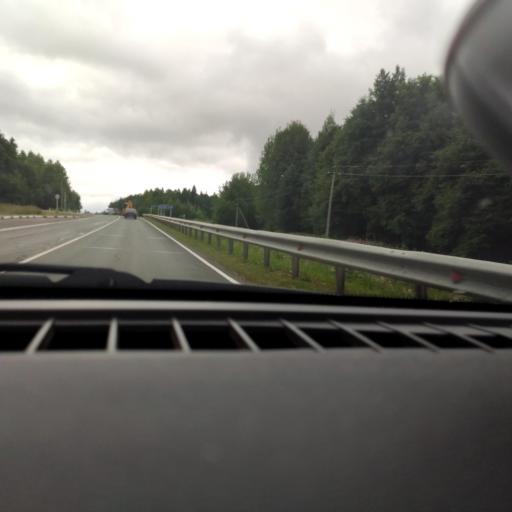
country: RU
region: Perm
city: Polazna
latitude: 58.3135
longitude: 56.1498
